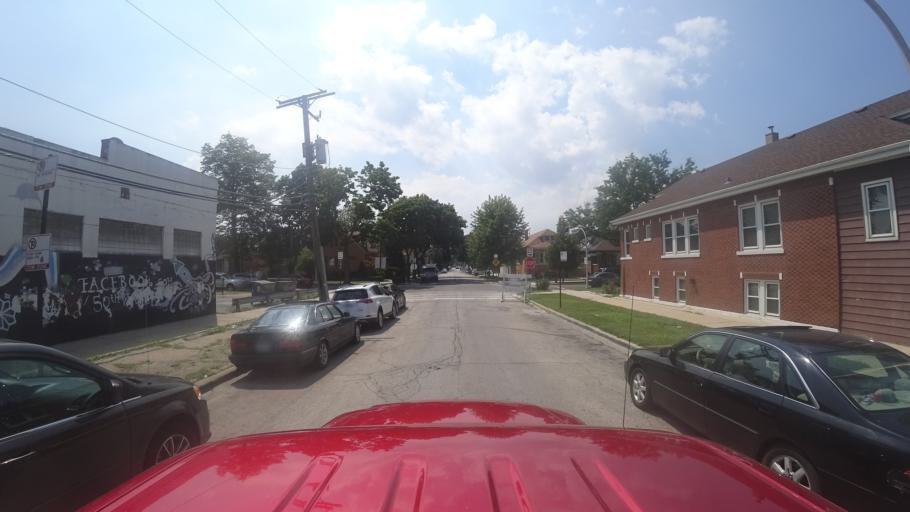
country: US
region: Illinois
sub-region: Cook County
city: Cicero
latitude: 41.8024
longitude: -87.7242
